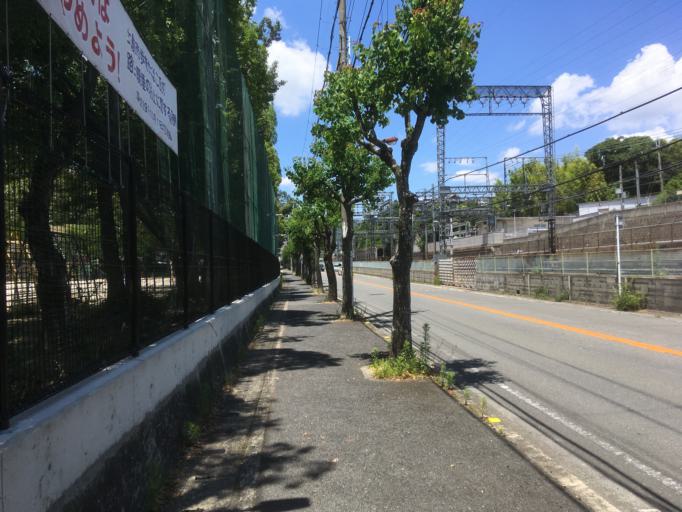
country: JP
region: Nara
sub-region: Ikoma-shi
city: Ikoma
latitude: 34.6923
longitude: 135.7072
